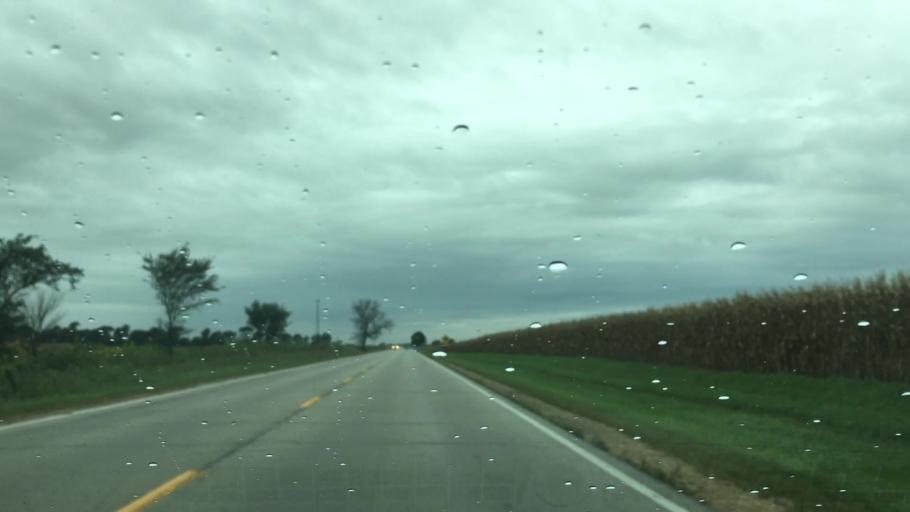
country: US
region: Illinois
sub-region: DeKalb County
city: Waterman
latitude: 41.7689
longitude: -88.8036
